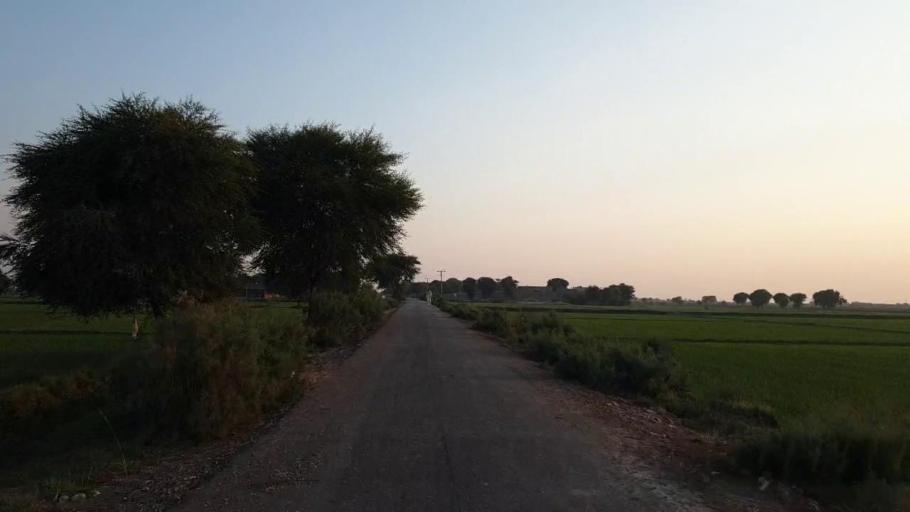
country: PK
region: Sindh
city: Sehwan
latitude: 26.4456
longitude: 67.7618
